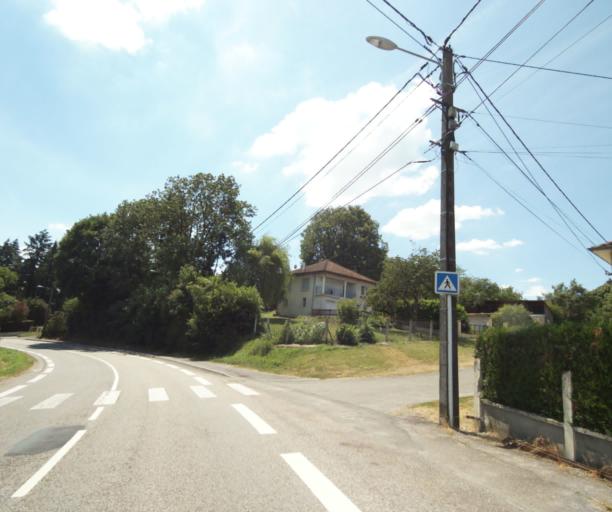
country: FR
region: Lorraine
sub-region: Departement de Meurthe-et-Moselle
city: Luneville
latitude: 48.6065
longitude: 6.4860
